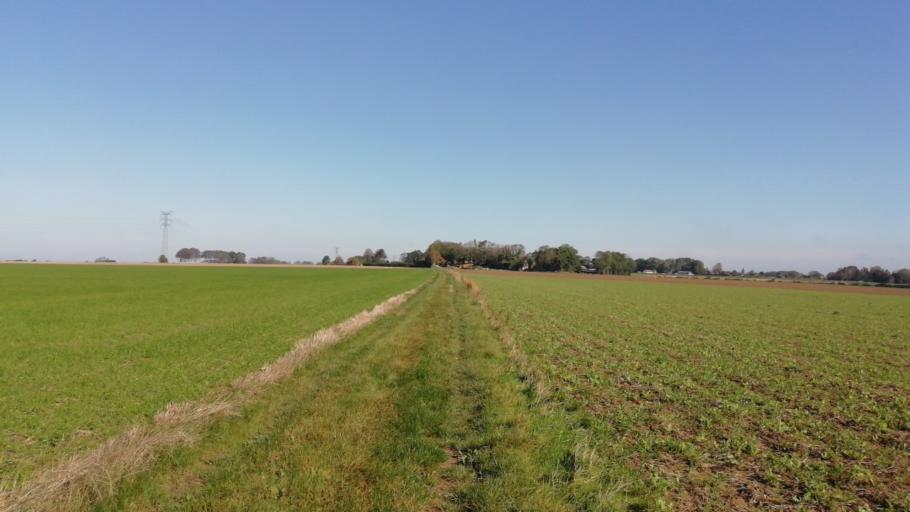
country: FR
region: Haute-Normandie
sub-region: Departement de la Seine-Maritime
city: Maneglise
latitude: 49.5811
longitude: 0.2642
